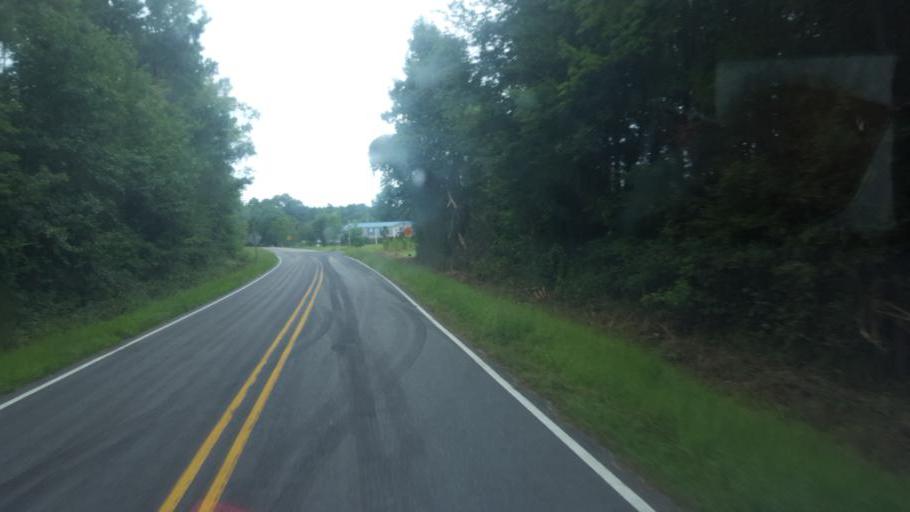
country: US
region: North Carolina
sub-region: Tyrrell County
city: Columbia
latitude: 35.9466
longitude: -76.3044
